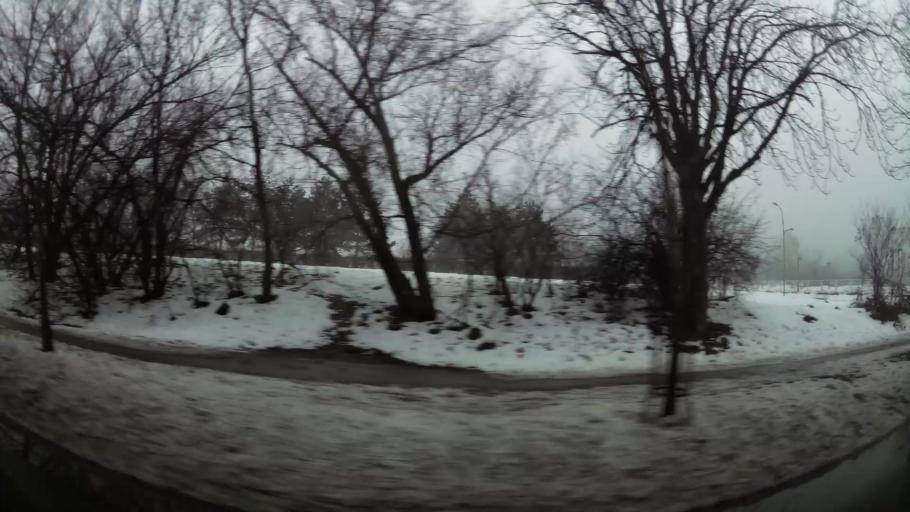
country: RS
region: Central Serbia
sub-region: Belgrade
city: Vozdovac
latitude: 44.7633
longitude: 20.4723
